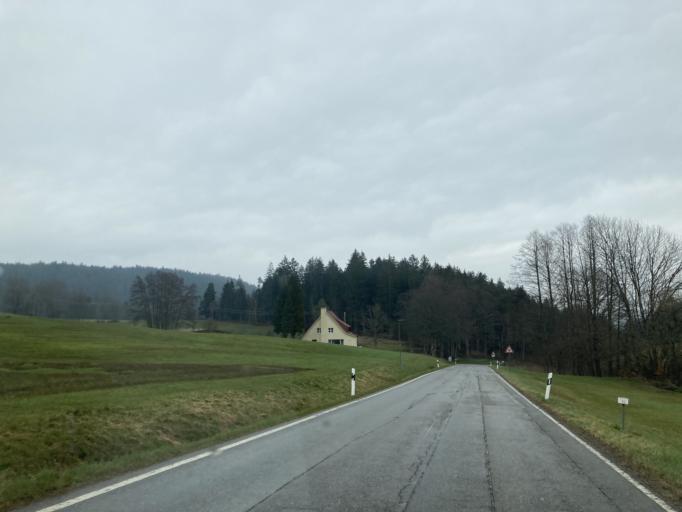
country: DE
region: Baden-Wuerttemberg
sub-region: Freiburg Region
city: Lauterbach/Schwarzwald
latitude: 48.2351
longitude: 8.2967
